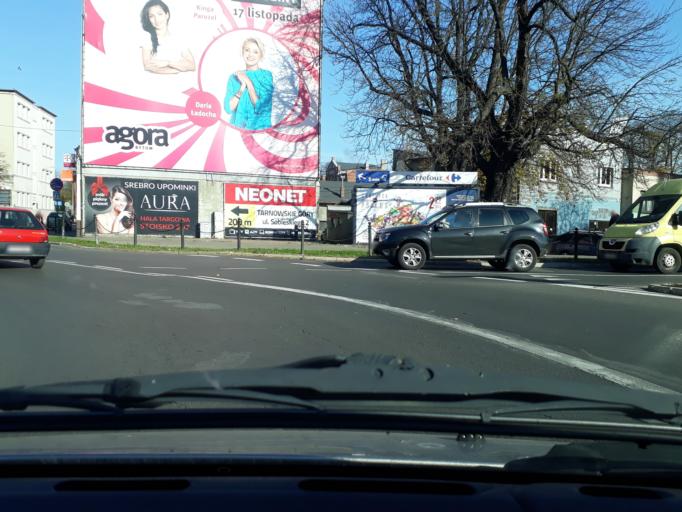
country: PL
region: Silesian Voivodeship
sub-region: Powiat tarnogorski
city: Tarnowskie Gory
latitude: 50.4455
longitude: 18.8616
